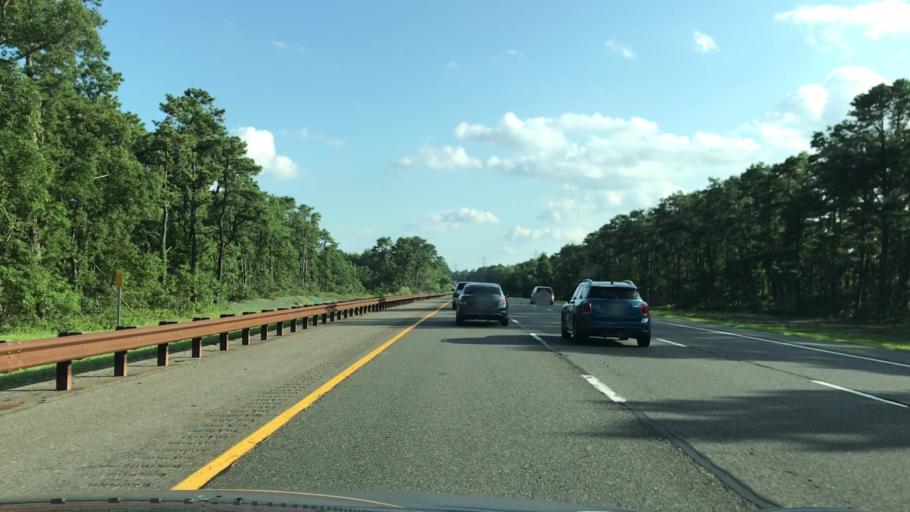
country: US
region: New Jersey
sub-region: Ocean County
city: Forked River
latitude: 39.8332
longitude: -74.2259
